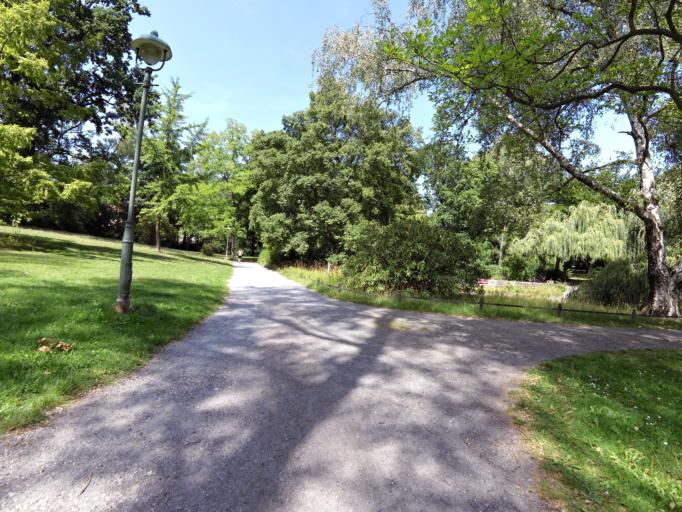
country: DE
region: Berlin
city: Steglitz Bezirk
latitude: 52.4489
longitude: 13.3348
